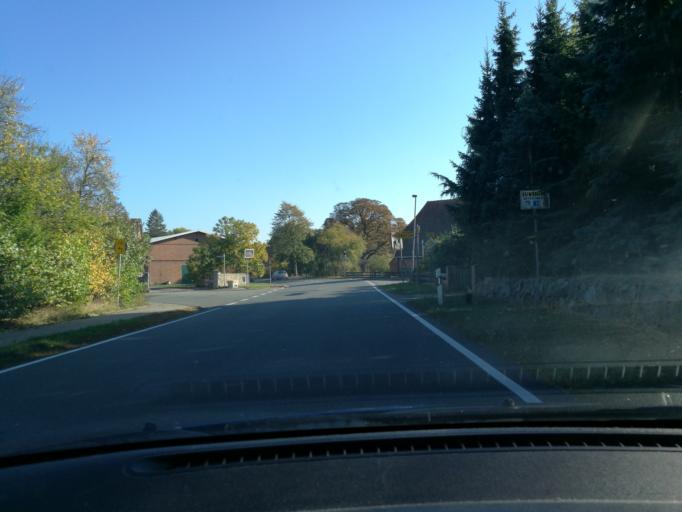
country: DE
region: Lower Saxony
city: Nahrendorf
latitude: 53.1594
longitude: 10.8083
